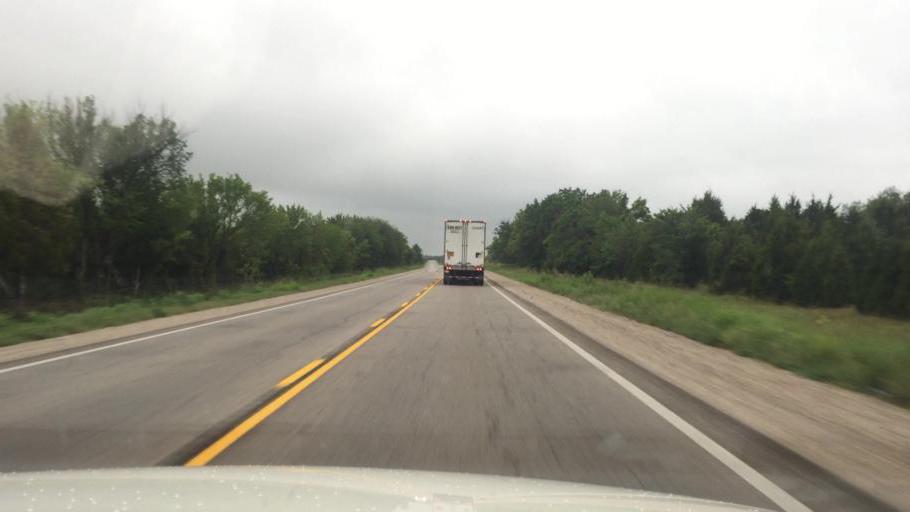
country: US
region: Kansas
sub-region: Montgomery County
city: Coffeyville
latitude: 37.1445
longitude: -95.5769
